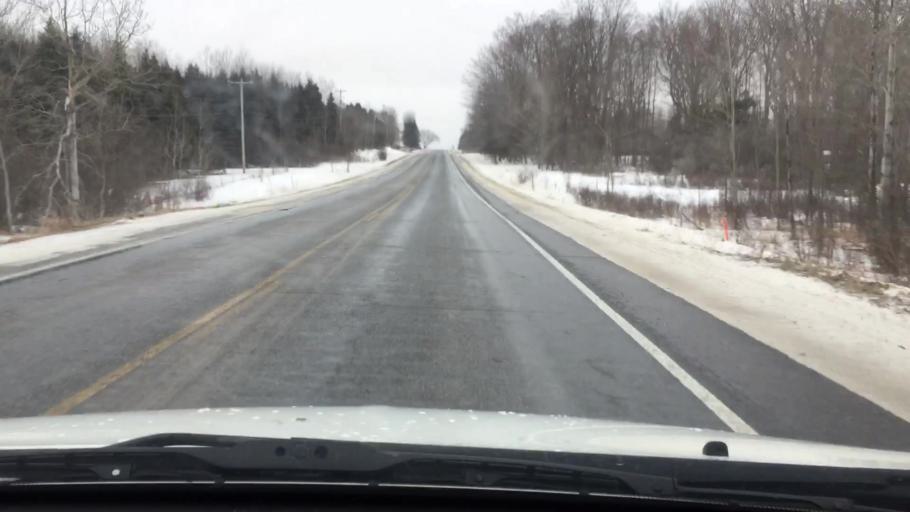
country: US
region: Michigan
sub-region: Osceola County
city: Reed City
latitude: 44.0499
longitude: -85.4439
